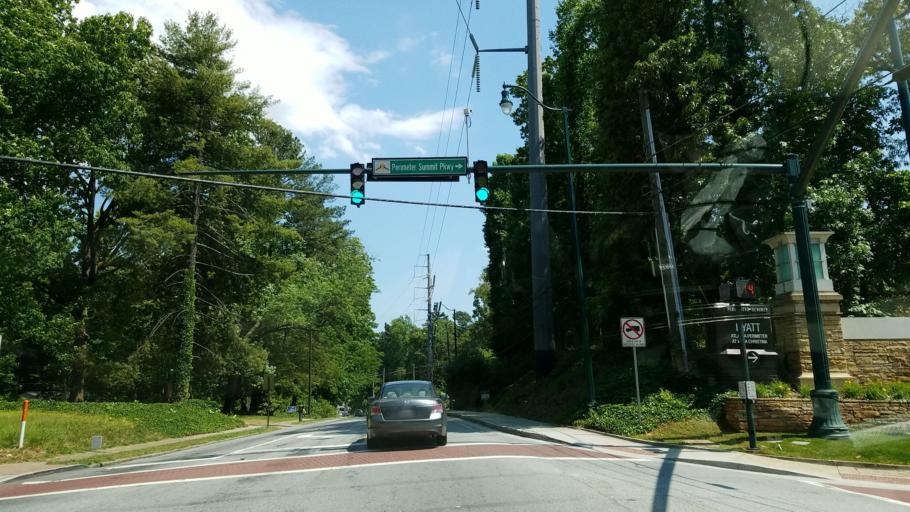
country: US
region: Georgia
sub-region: DeKalb County
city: Dunwoody
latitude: 33.9137
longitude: -84.3358
